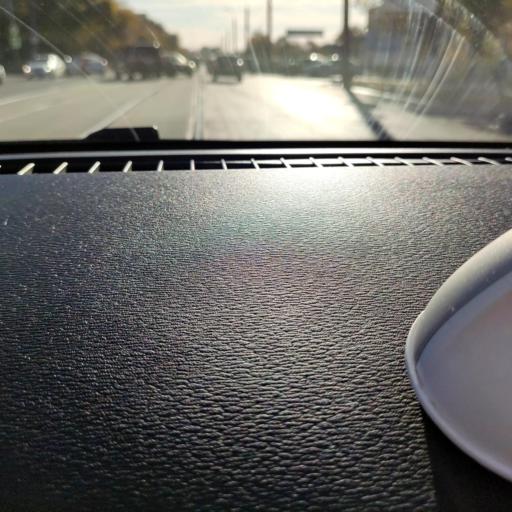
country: RU
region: Samara
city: Samara
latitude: 53.1966
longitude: 50.1577
